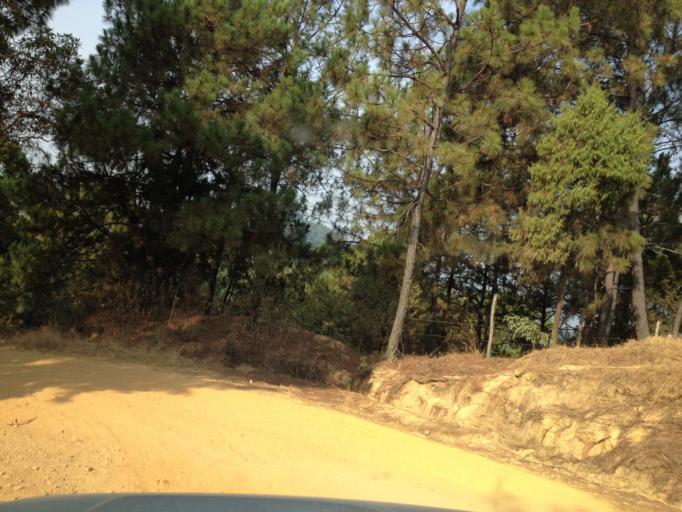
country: MX
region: Michoacan
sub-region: Zitacuaro
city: Macutzio
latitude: 19.4967
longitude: -100.3218
